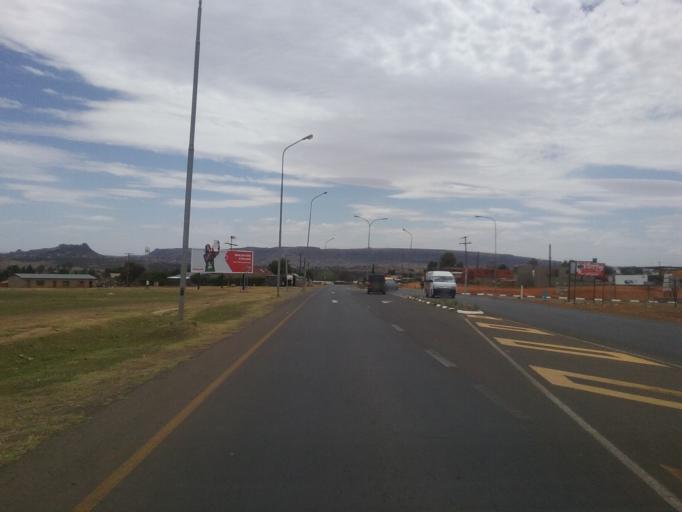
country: LS
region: Maseru
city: Maseru
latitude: -29.4238
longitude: 27.5619
